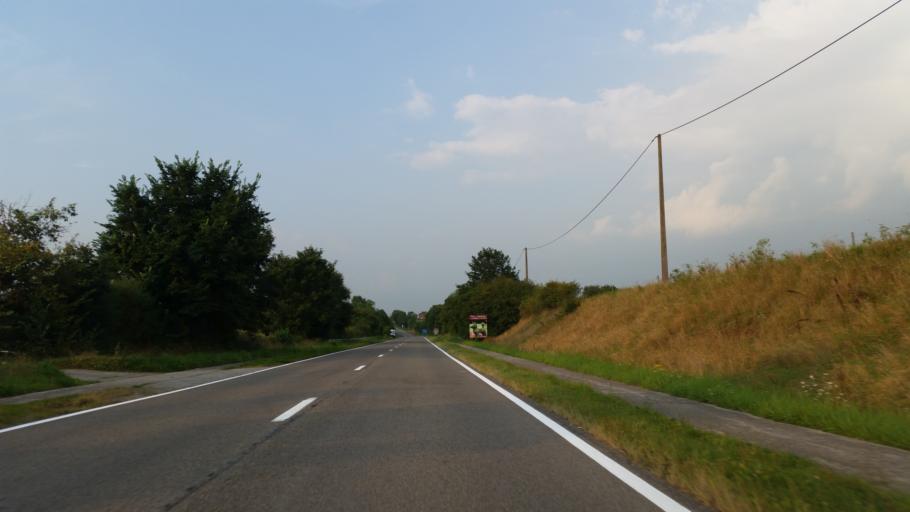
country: BE
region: Wallonia
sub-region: Province de Namur
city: Somme-Leuze
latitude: 50.3192
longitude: 5.4139
